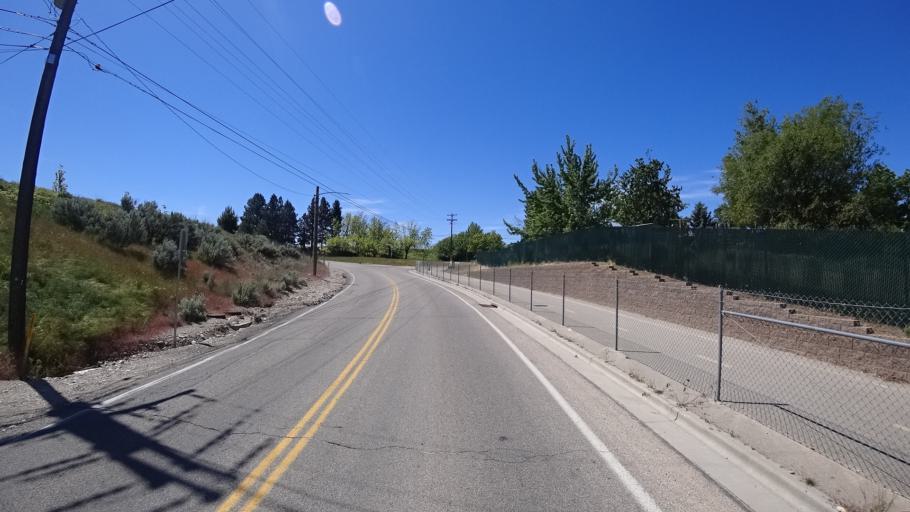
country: US
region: Idaho
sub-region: Ada County
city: Boise
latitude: 43.5648
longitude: -116.1333
